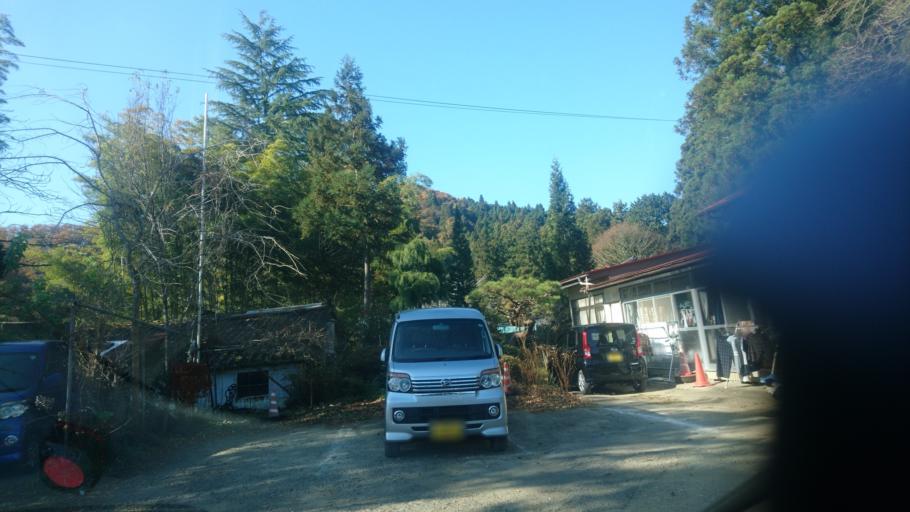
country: JP
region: Miyagi
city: Okawara
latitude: 38.1329
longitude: 140.7501
